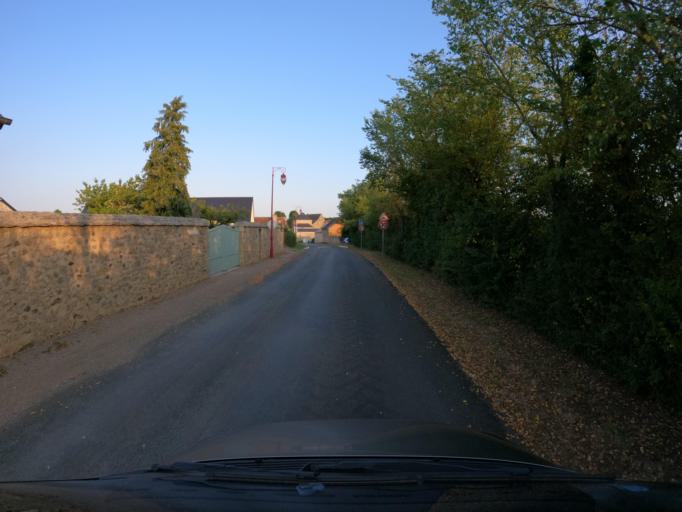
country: FR
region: Pays de la Loire
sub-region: Departement de la Sarthe
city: Brulon
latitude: 47.9057
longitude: -0.2220
